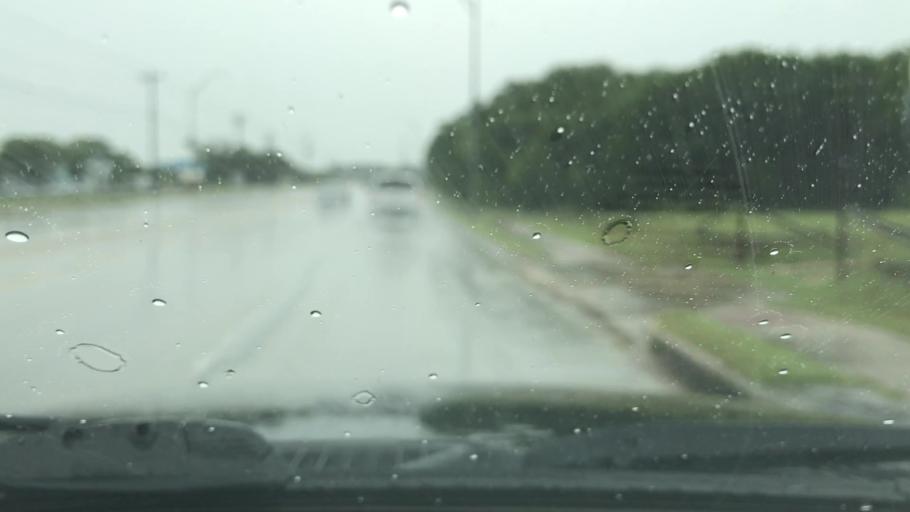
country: US
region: Texas
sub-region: Williamson County
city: Cedar Park
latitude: 30.4947
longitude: -97.8253
